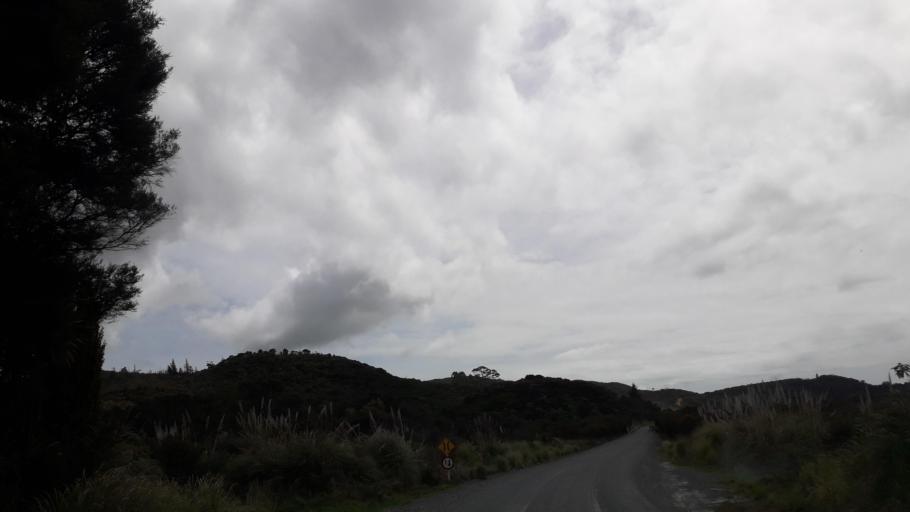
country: NZ
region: Northland
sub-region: Far North District
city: Taipa
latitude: -35.0298
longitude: 173.5607
